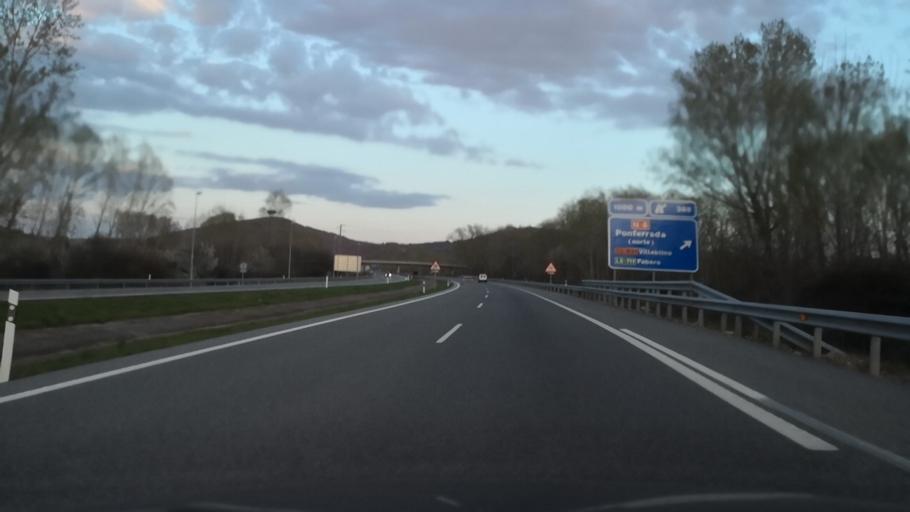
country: ES
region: Castille and Leon
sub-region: Provincia de Leon
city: Camponaraya
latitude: 42.5831
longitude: -6.6236
